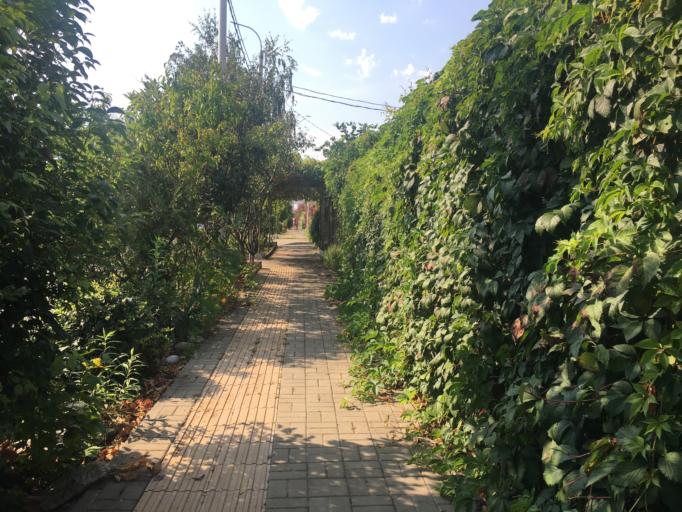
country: RU
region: Krasnodarskiy
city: Vysokoye
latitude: 43.3926
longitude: 40.0008
